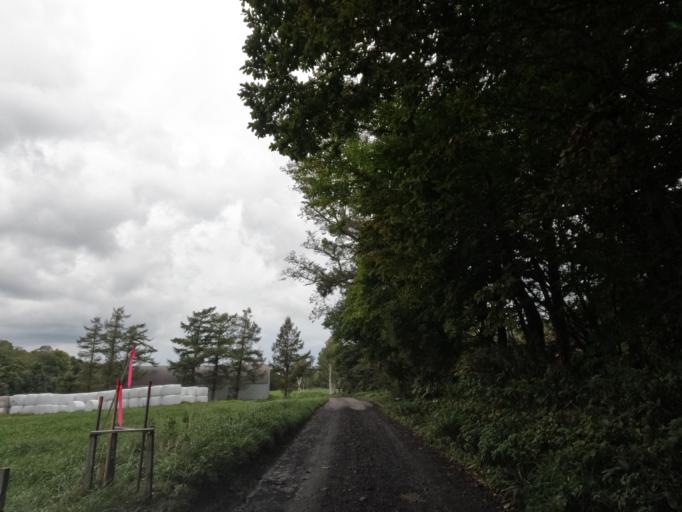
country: JP
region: Hokkaido
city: Date
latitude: 42.5009
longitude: 140.9086
